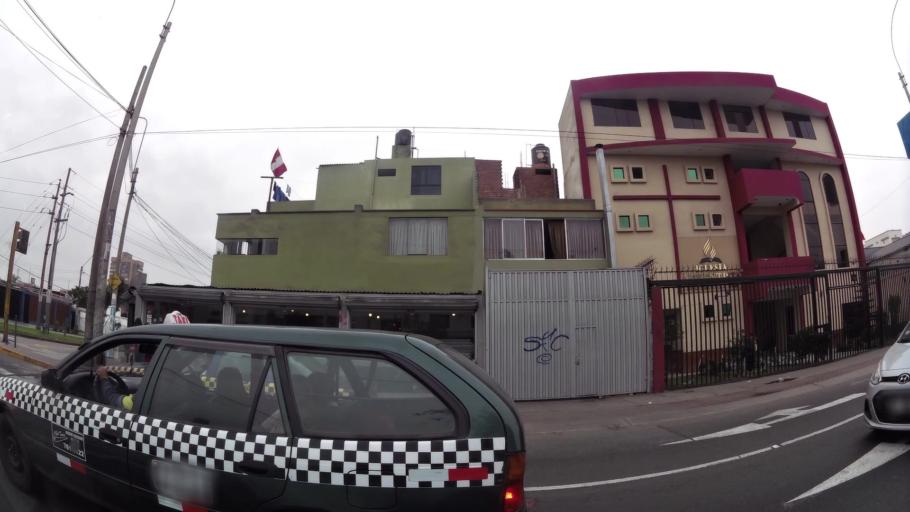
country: PE
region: Lima
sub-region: Lima
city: San Luis
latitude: -12.0850
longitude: -77.0102
